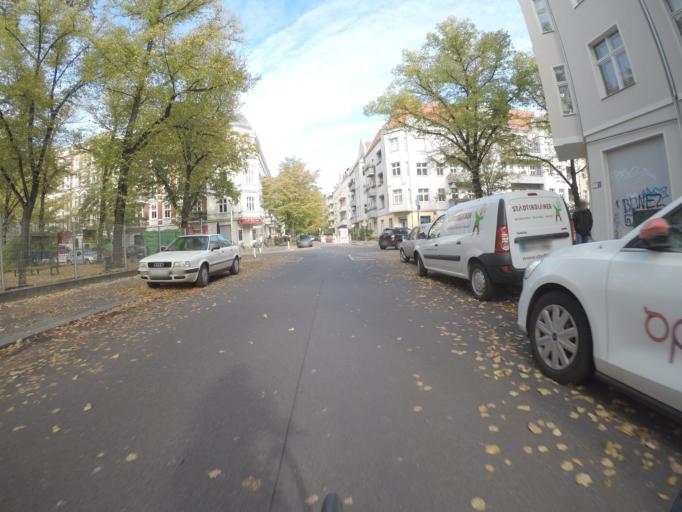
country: DE
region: Berlin
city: Tempelhof Bezirk
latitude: 52.4582
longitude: 13.3816
